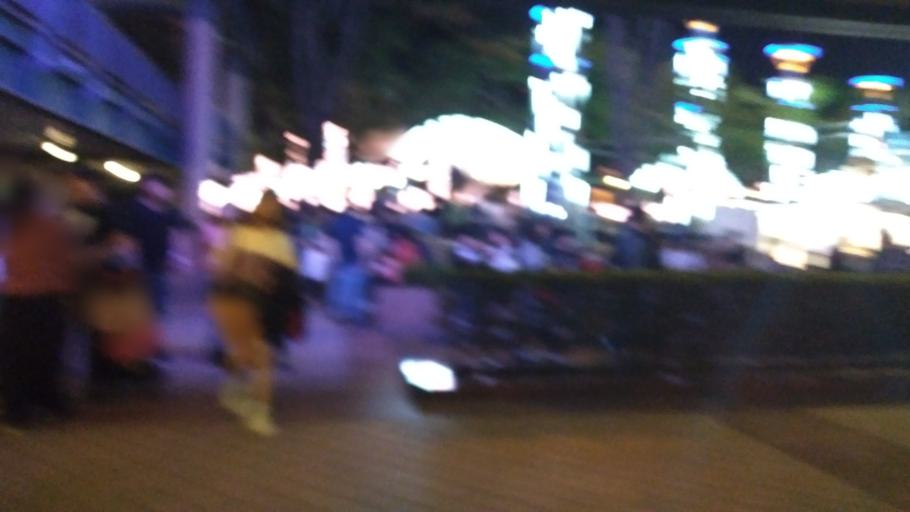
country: TW
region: Taipei
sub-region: Taipei
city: Banqiao
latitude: 25.0130
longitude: 121.4647
